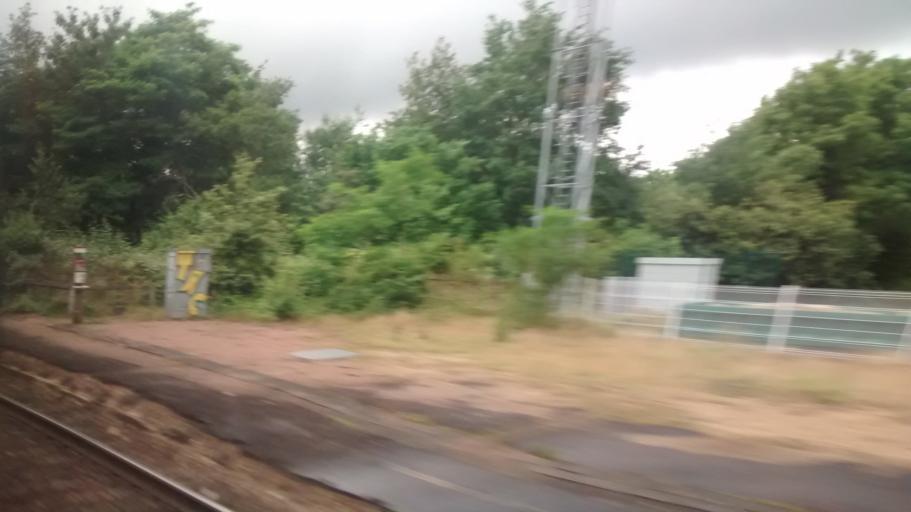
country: FR
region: Pays de la Loire
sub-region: Departement de la Sarthe
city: Change
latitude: 48.0076
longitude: 0.2805
